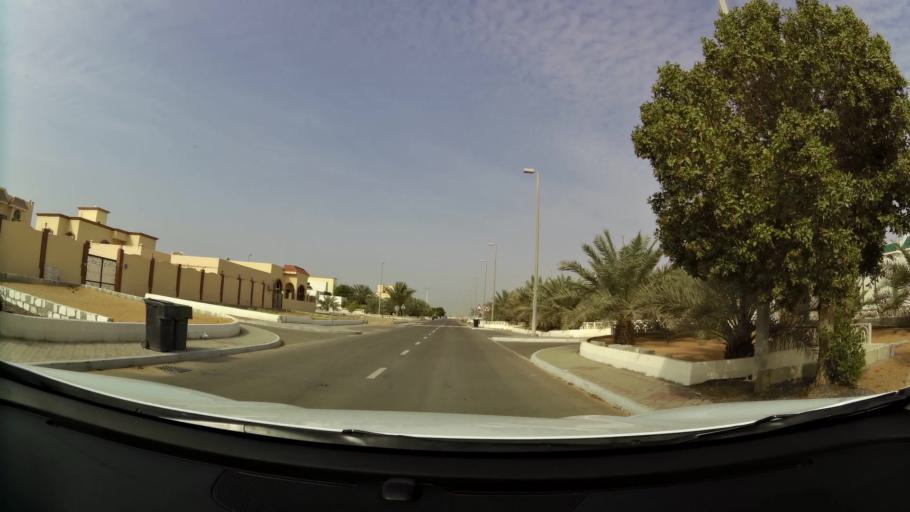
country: AE
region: Abu Dhabi
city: Abu Dhabi
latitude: 24.6123
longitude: 54.7043
